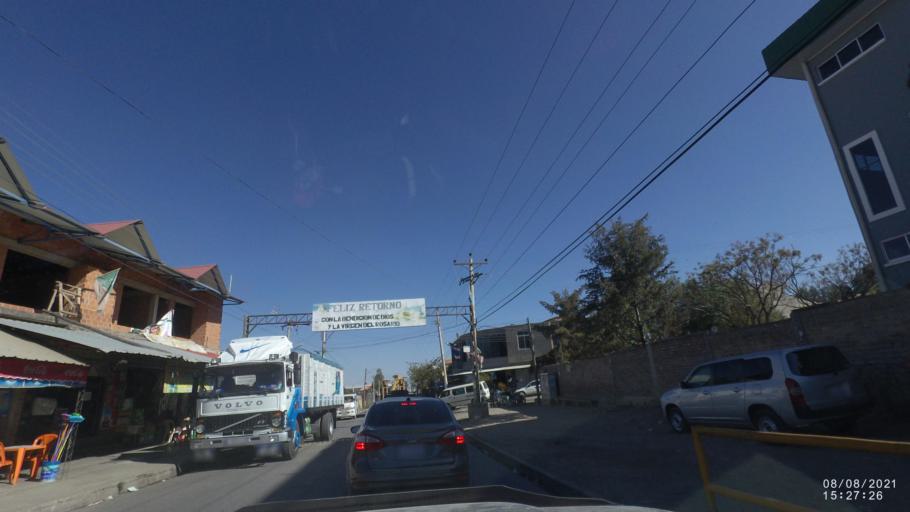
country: BO
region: Cochabamba
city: Cochabamba
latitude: -17.3295
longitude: -66.2827
